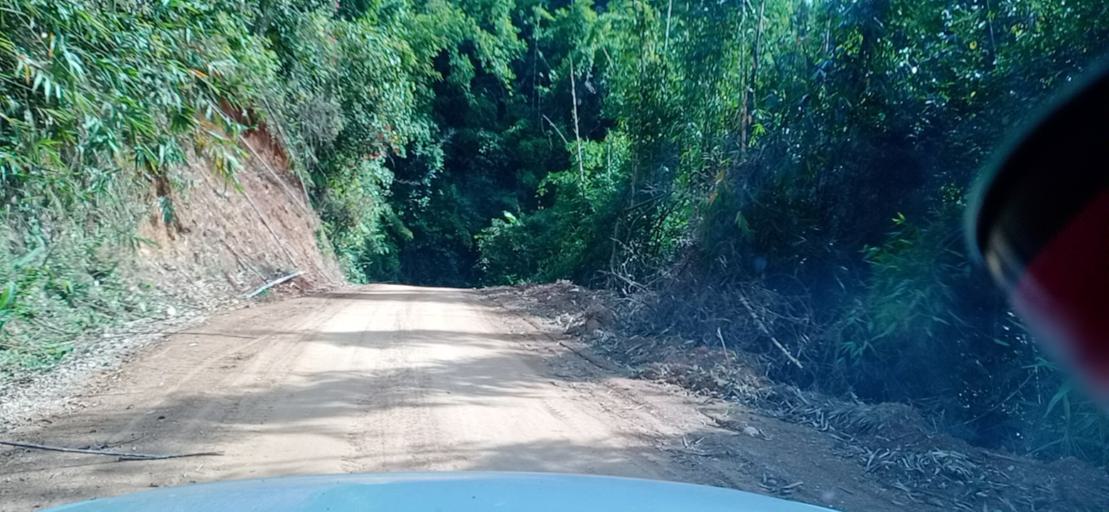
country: TH
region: Changwat Bueng Kan
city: Pak Khat
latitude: 18.6382
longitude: 103.2455
